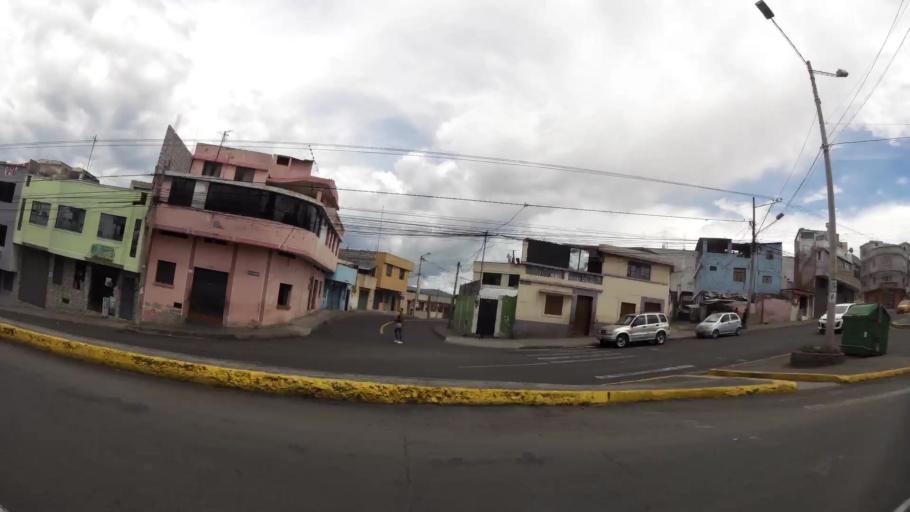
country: EC
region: Tungurahua
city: Ambato
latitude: -1.2509
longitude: -78.6224
